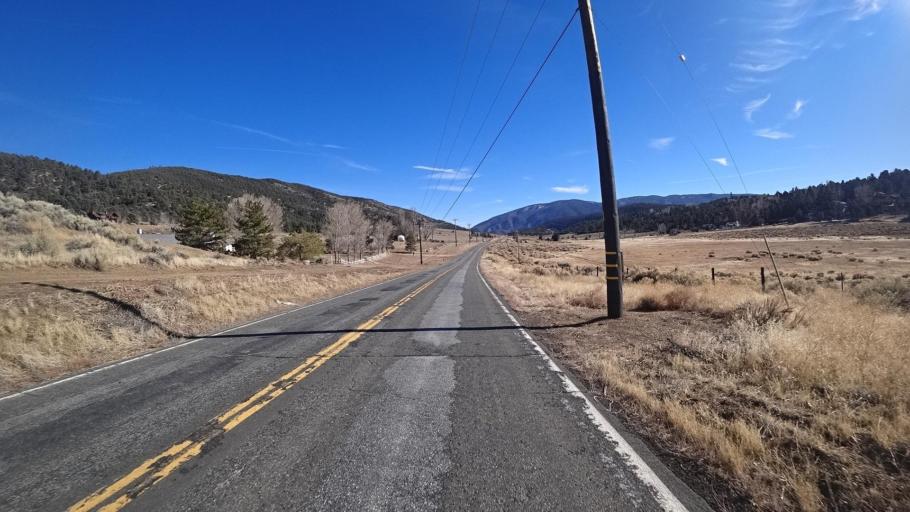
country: US
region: California
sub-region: Kern County
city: Frazier Park
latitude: 34.8373
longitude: -119.0447
